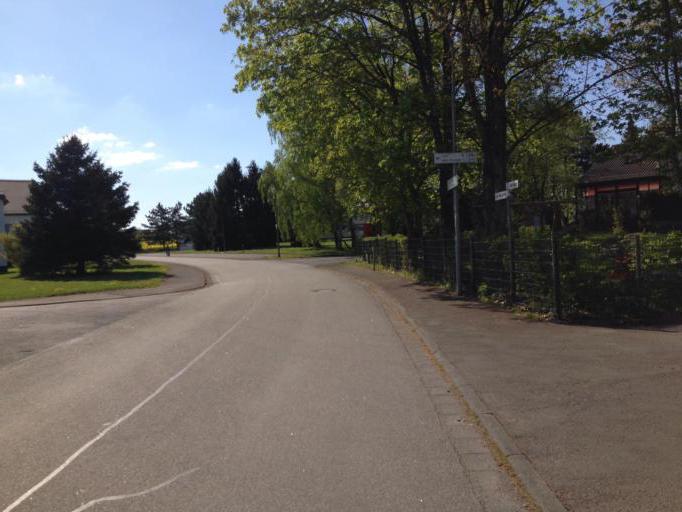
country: DE
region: Hesse
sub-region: Regierungsbezirk Giessen
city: Grunberg
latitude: 50.5598
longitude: 8.8959
